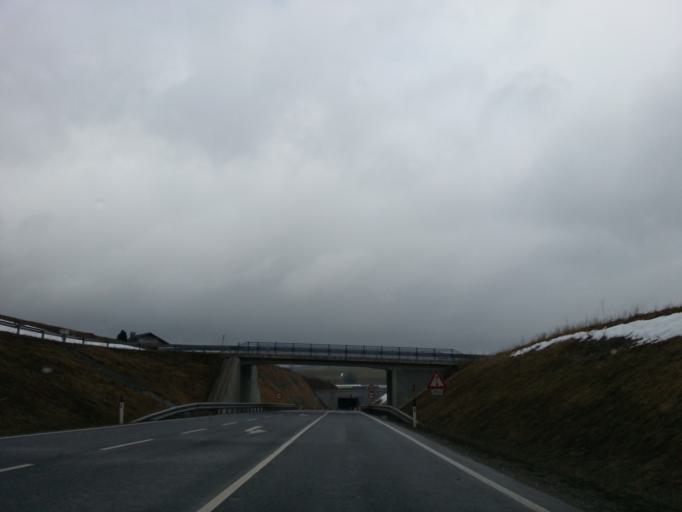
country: AT
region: Salzburg
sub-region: Politischer Bezirk Salzburg-Umgebung
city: Strasswalchen
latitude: 47.9767
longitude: 13.2436
